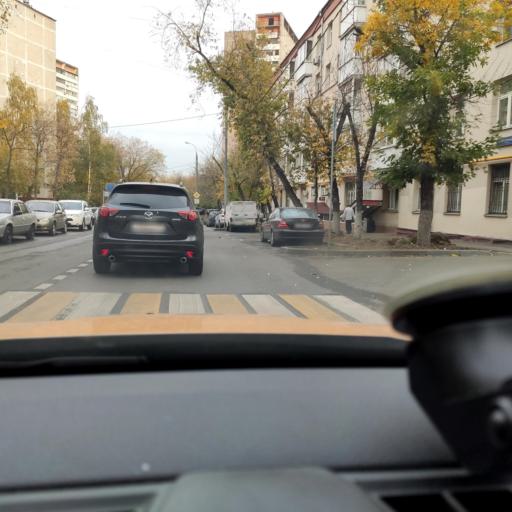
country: RU
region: Moscow
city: Tekstil'shchiki
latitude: 55.7047
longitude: 37.7402
